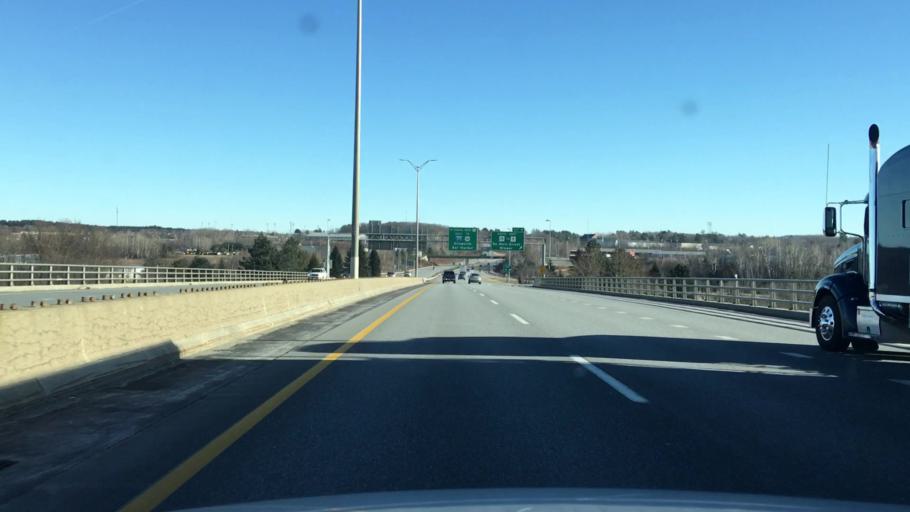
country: US
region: Maine
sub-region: Penobscot County
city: Bangor
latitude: 44.7840
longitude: -68.7737
